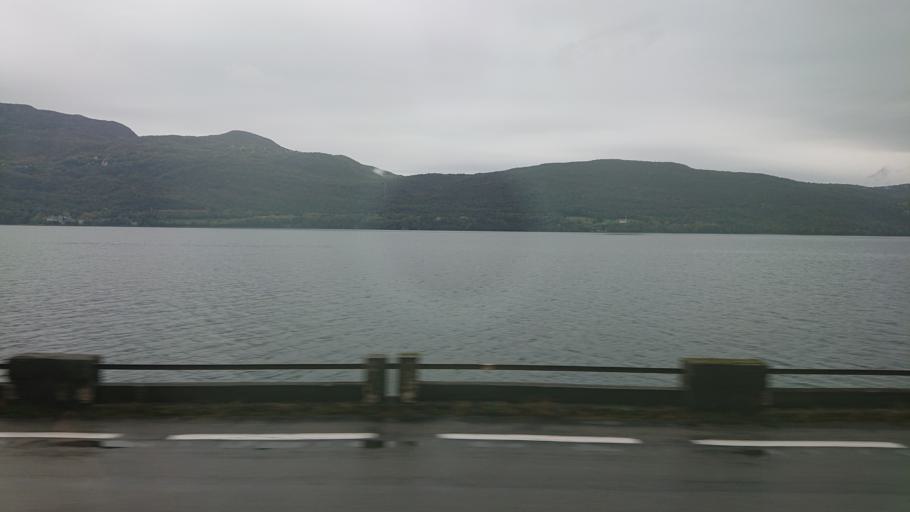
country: FR
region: Rhone-Alpes
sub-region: Departement de la Savoie
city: Chatillon
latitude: 45.7764
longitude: 5.8657
